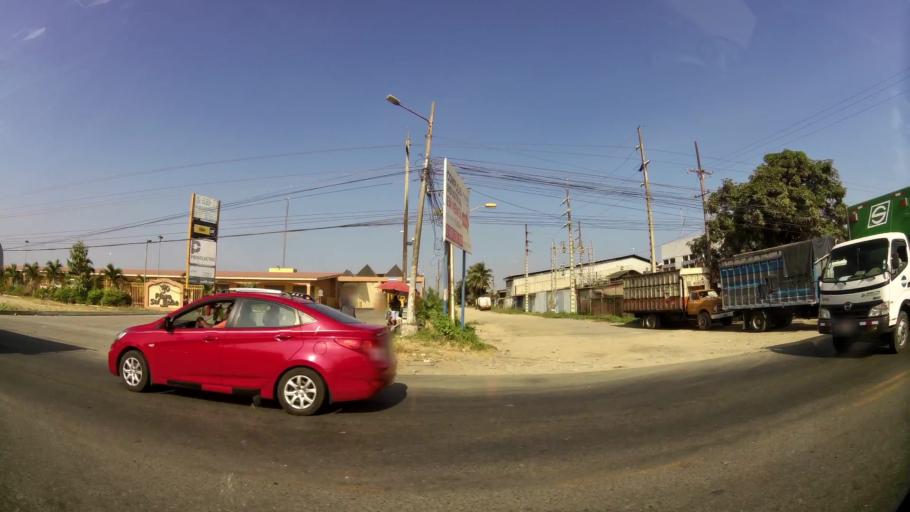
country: EC
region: Guayas
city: Eloy Alfaro
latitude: -2.1913
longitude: -79.8246
